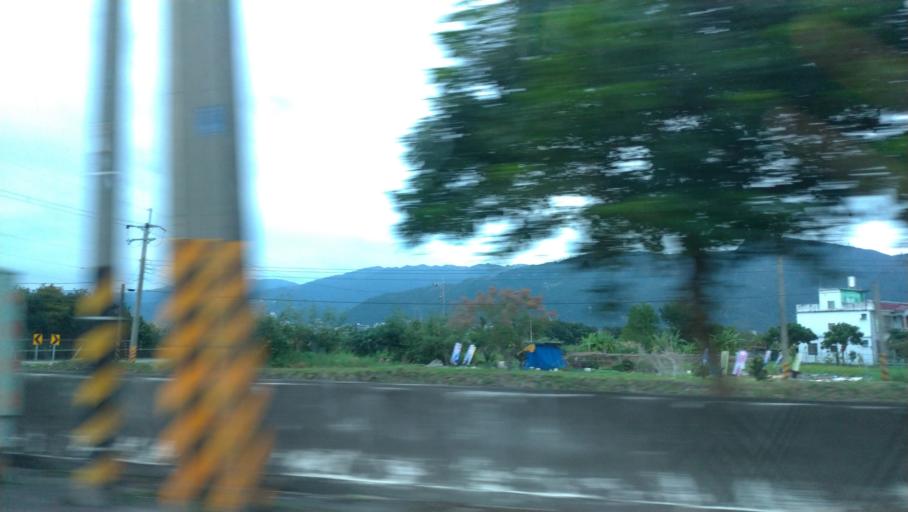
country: TW
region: Taiwan
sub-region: Yilan
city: Yilan
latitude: 24.8267
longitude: 121.8008
